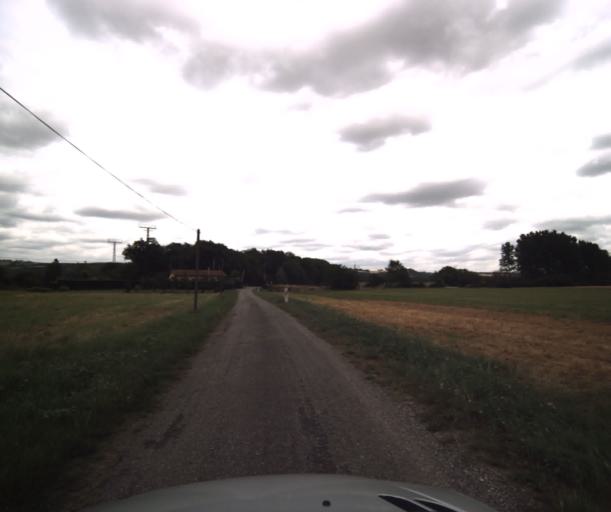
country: FR
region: Midi-Pyrenees
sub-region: Departement de la Haute-Garonne
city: Labarthe-sur-Leze
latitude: 43.4667
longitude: 1.4045
